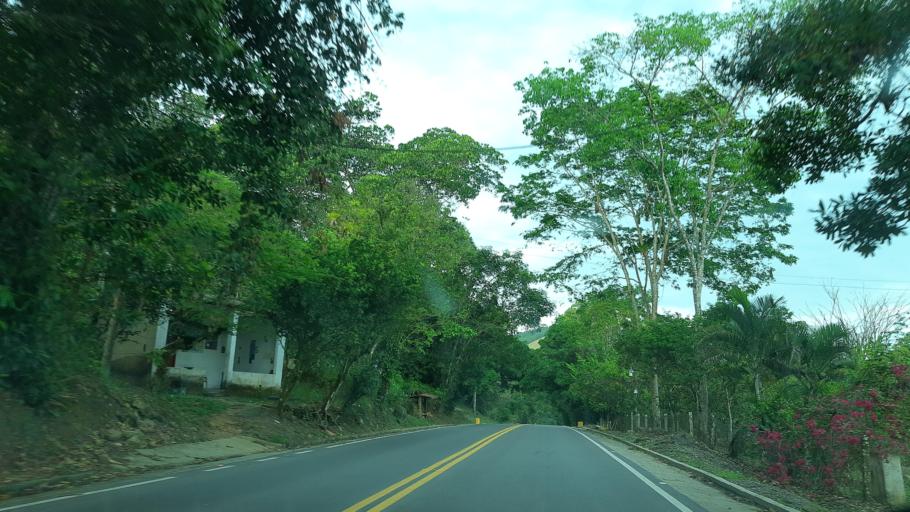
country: CO
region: Boyaca
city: San Luis de Gaceno
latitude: 4.8313
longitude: -73.1414
